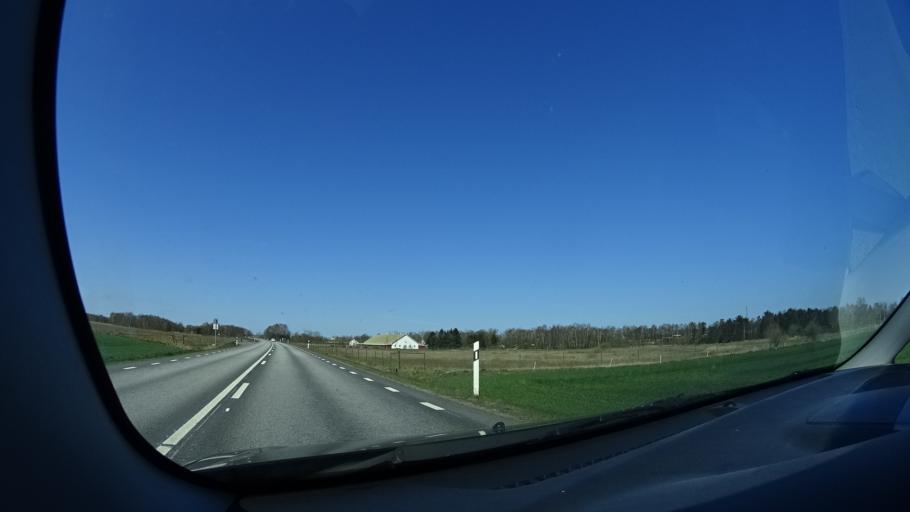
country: SE
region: Skane
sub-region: Hoganas Kommun
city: Hoganas
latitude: 56.2154
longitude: 12.6763
